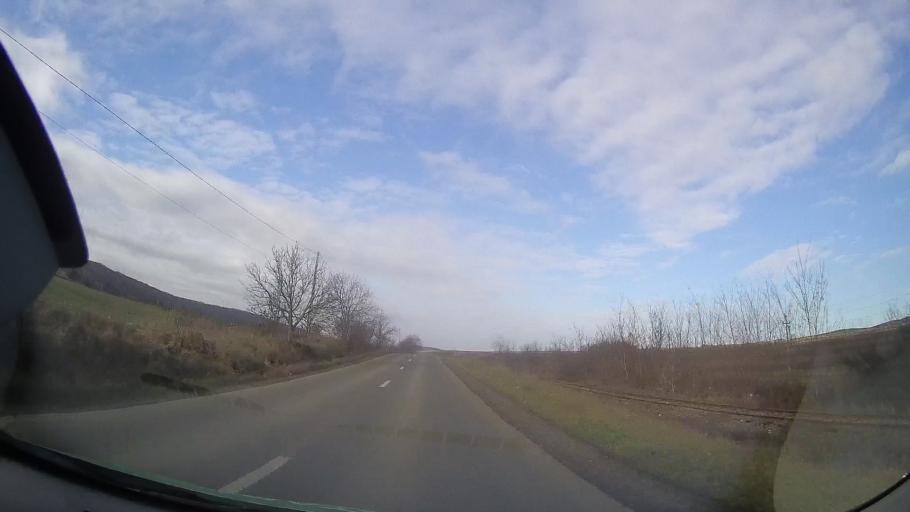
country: RO
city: Barza
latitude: 46.5510
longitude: 24.1144
